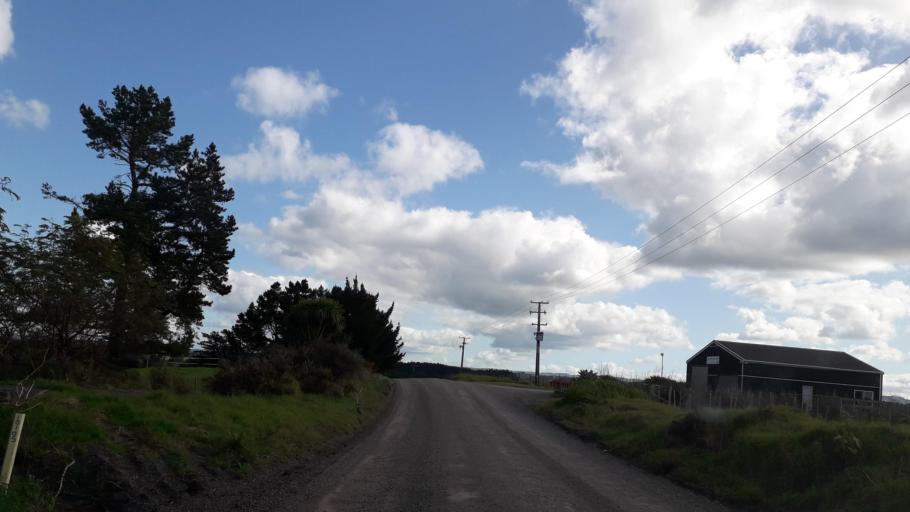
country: NZ
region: Northland
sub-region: Far North District
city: Kerikeri
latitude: -35.1332
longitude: 174.0004
